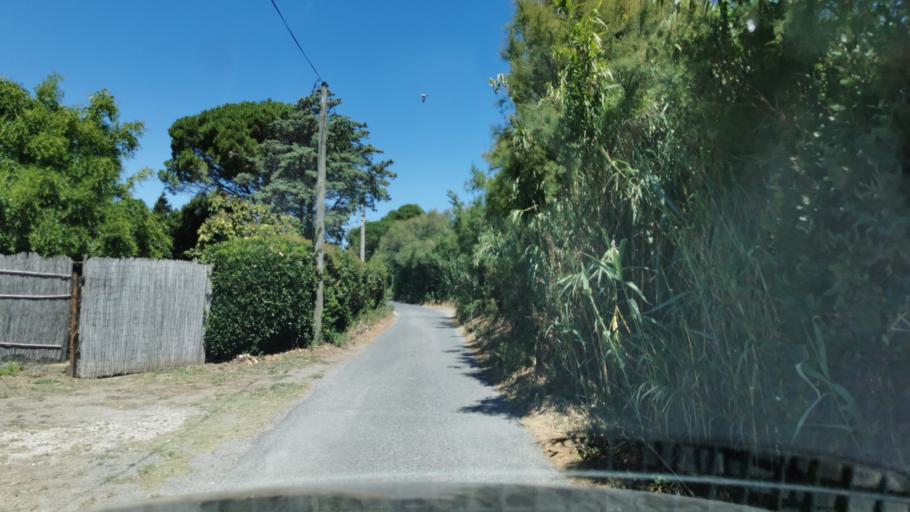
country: FR
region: Languedoc-Roussillon
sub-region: Departement de l'Aude
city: Peyriac-de-Mer
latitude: 43.0909
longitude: 2.9589
